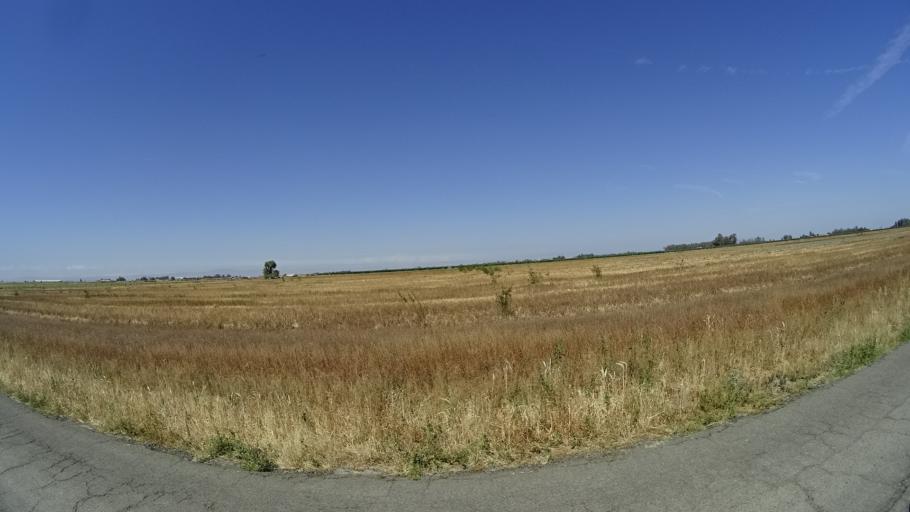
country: US
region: California
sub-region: Kings County
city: Stratford
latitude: 36.1831
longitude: -119.7803
